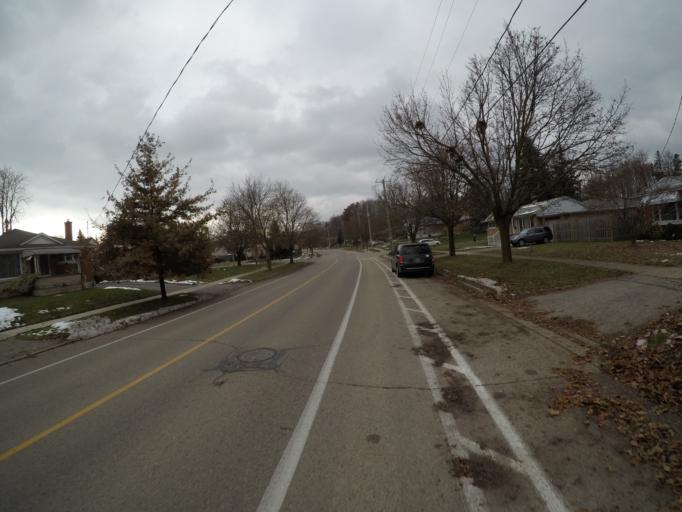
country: CA
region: Ontario
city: Waterloo
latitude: 43.4713
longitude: -80.4880
